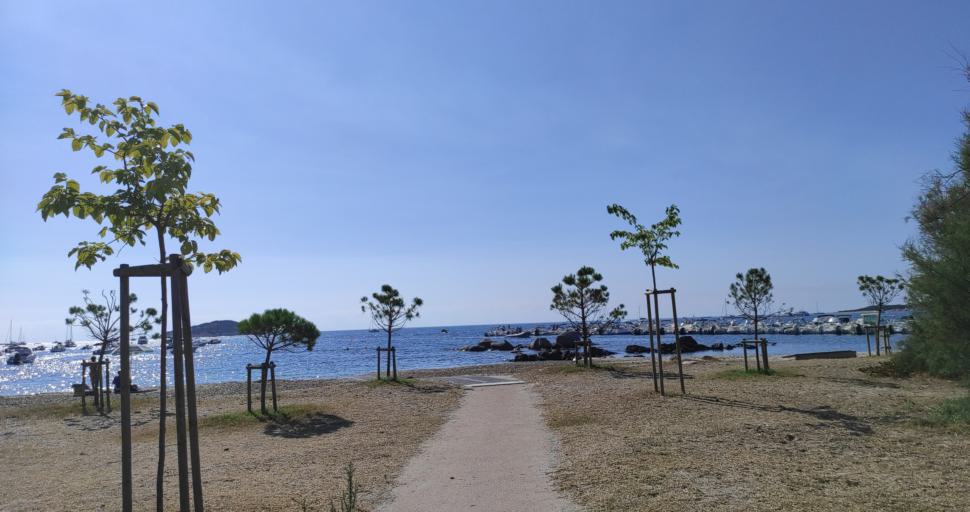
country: FR
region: Corsica
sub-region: Departement de la Corse-du-Sud
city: Porto-Vecchio
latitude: 41.6374
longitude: 9.3476
